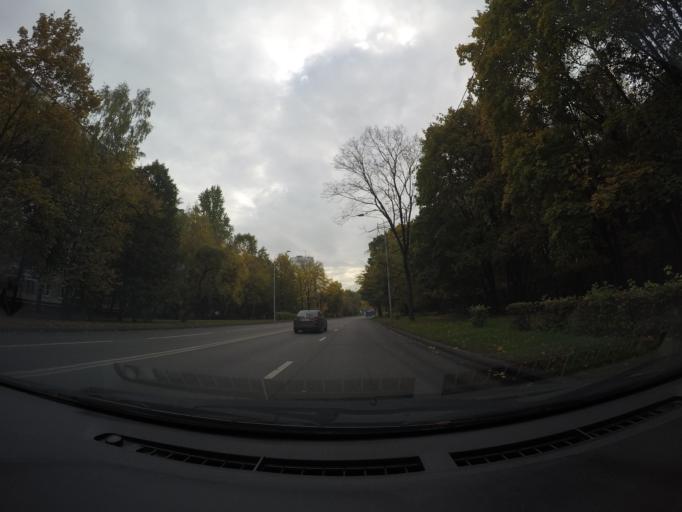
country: RU
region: Moskovskaya
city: Novogireyevo
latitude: 55.7643
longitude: 37.8223
